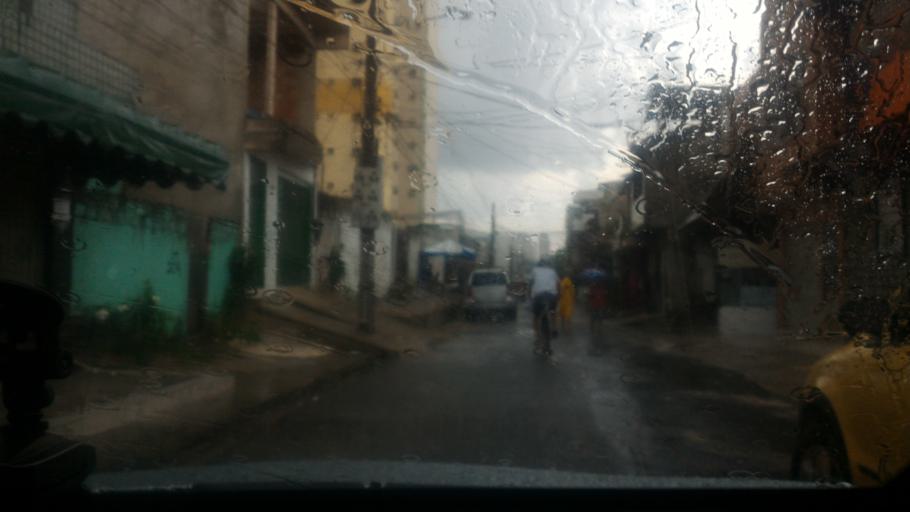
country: BR
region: Para
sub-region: Belem
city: Belem
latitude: -1.4363
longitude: -48.4768
